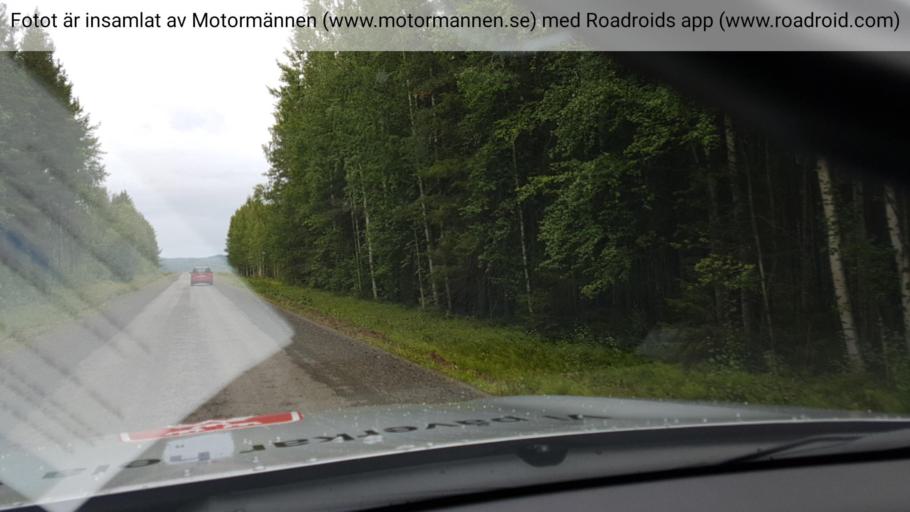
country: SE
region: Norrbotten
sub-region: Alvsbyns Kommun
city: AElvsbyn
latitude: 65.9764
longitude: 21.2161
